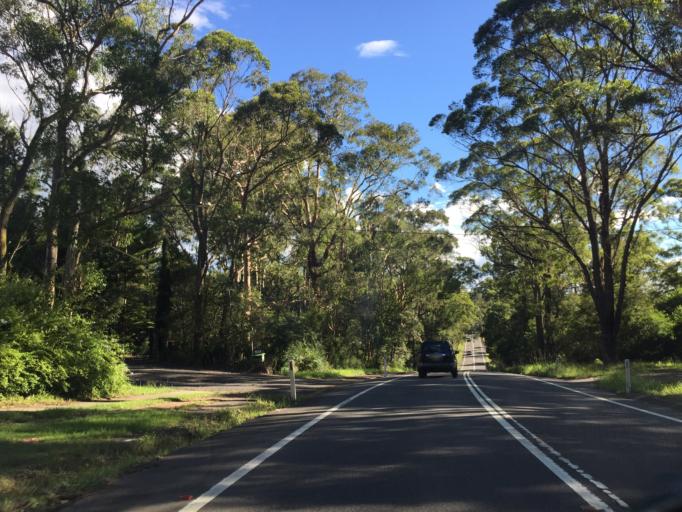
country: AU
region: New South Wales
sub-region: Hornsby Shire
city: Galston
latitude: -33.6627
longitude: 151.0392
